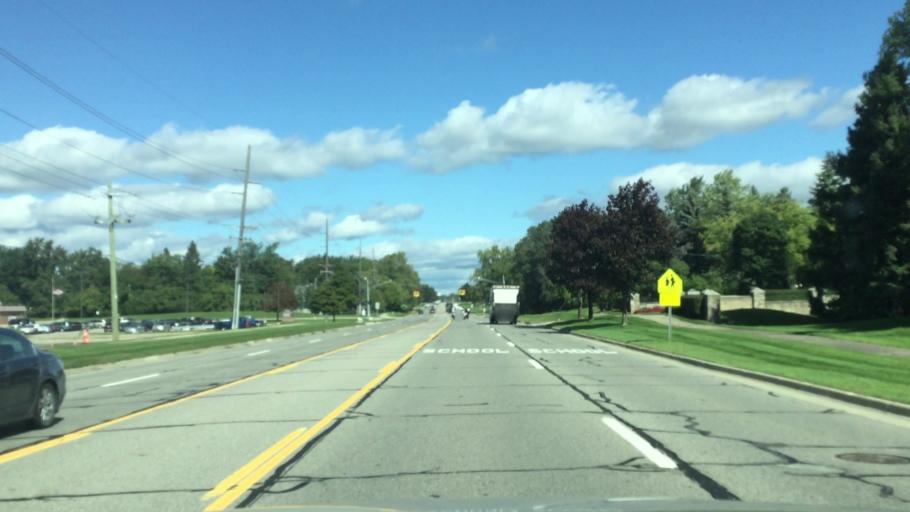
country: US
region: Michigan
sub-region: Oakland County
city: West Bloomfield Township
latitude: 42.5485
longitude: -83.3609
